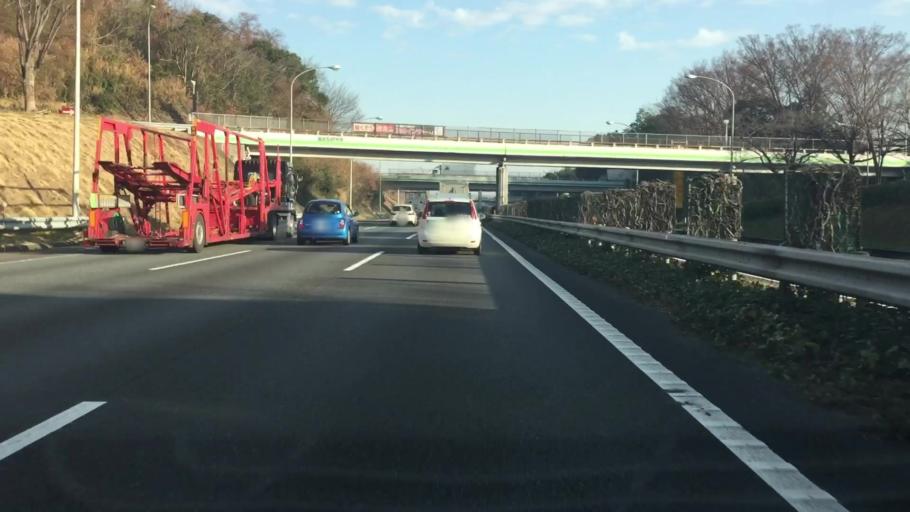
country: JP
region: Saitama
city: Sakado
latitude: 35.9867
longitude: 139.3826
